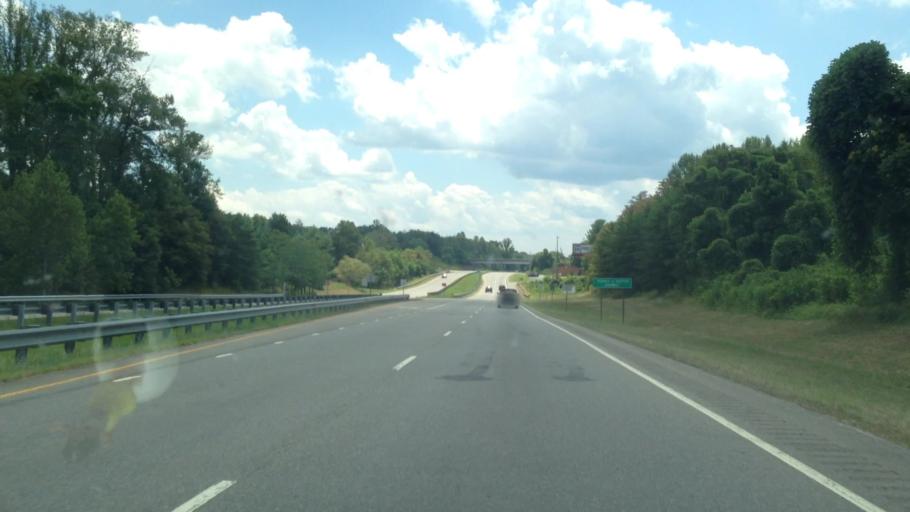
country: US
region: North Carolina
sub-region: Rockingham County
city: Stoneville
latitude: 36.5381
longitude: -79.9133
